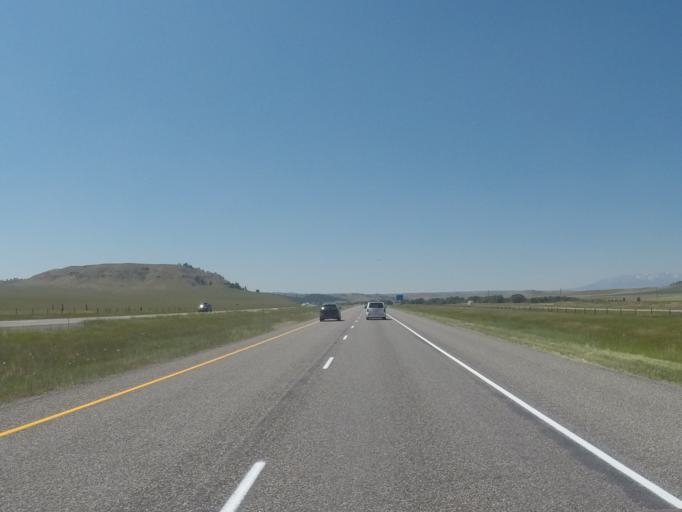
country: US
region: Montana
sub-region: Sweet Grass County
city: Big Timber
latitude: 45.7344
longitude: -109.7082
